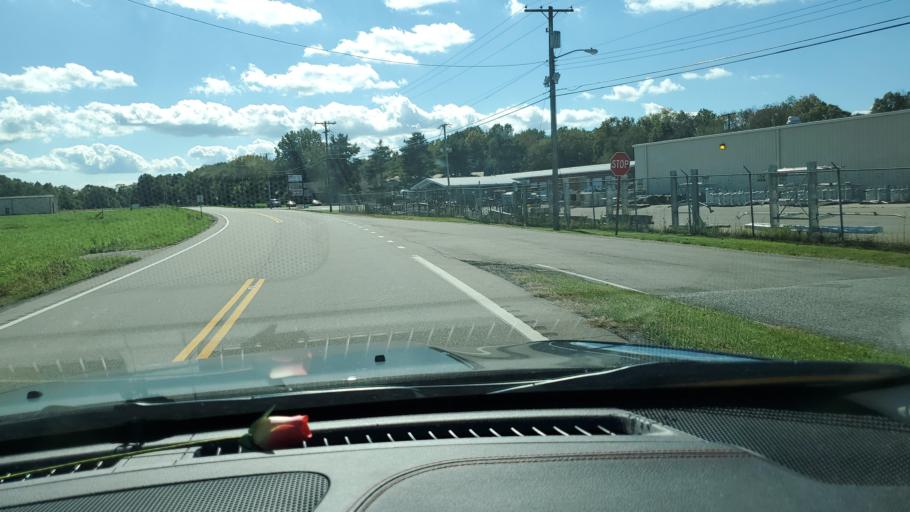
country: US
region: Ohio
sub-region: Trumbull County
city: Cortland
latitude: 41.4382
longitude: -80.5998
